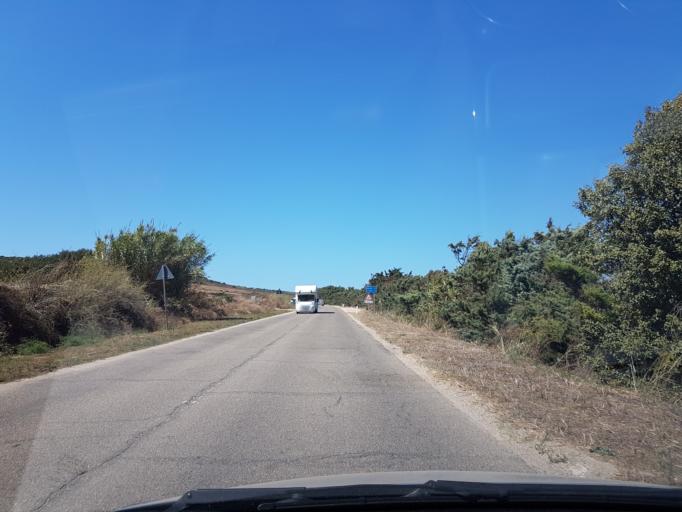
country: IT
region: Sardinia
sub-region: Provincia di Oristano
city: Cabras
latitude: 39.9325
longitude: 8.4574
